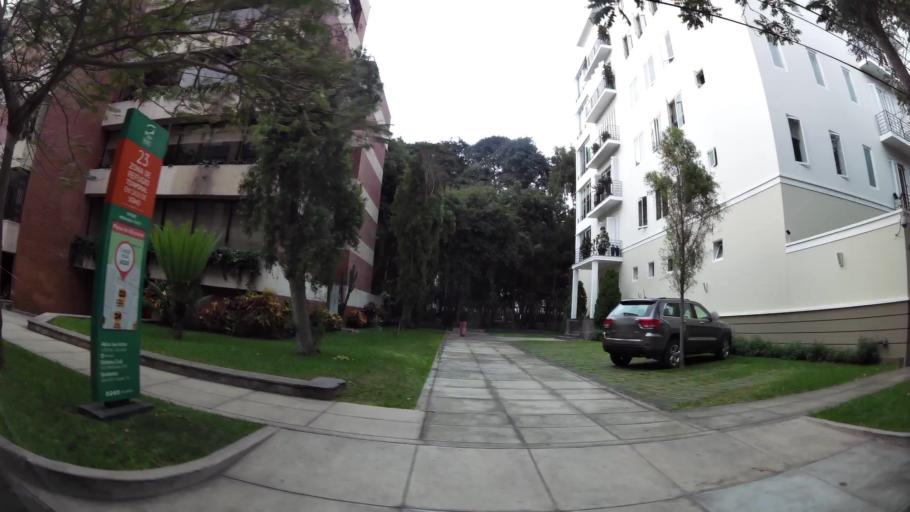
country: PE
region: Lima
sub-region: Lima
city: San Isidro
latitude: -12.1061
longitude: -77.0451
